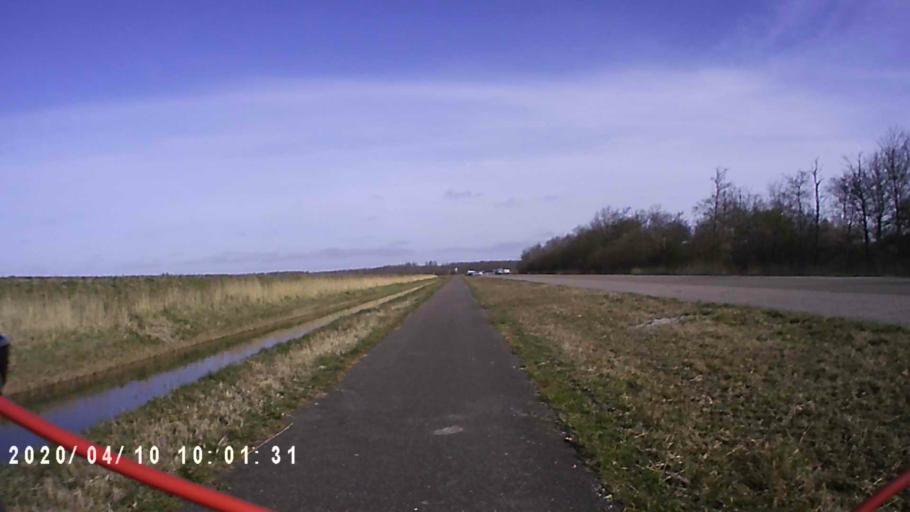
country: NL
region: Groningen
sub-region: Gemeente De Marne
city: Ulrum
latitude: 53.3619
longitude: 6.2607
